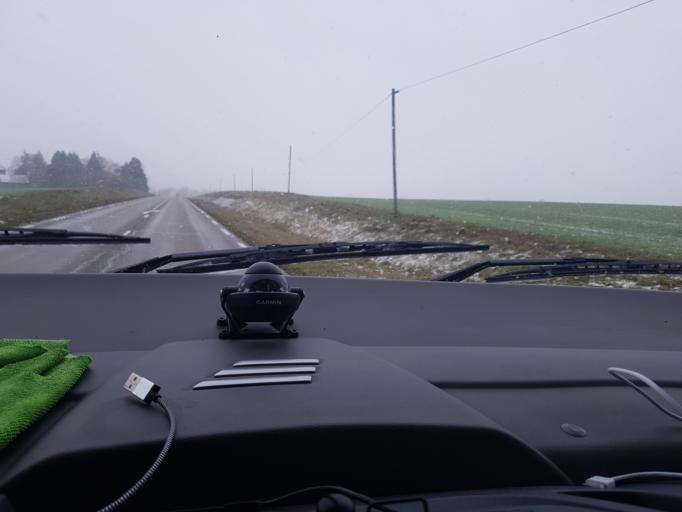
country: FR
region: Lorraine
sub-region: Departement de la Moselle
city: Vic-sur-Seille
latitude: 48.7874
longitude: 6.5650
